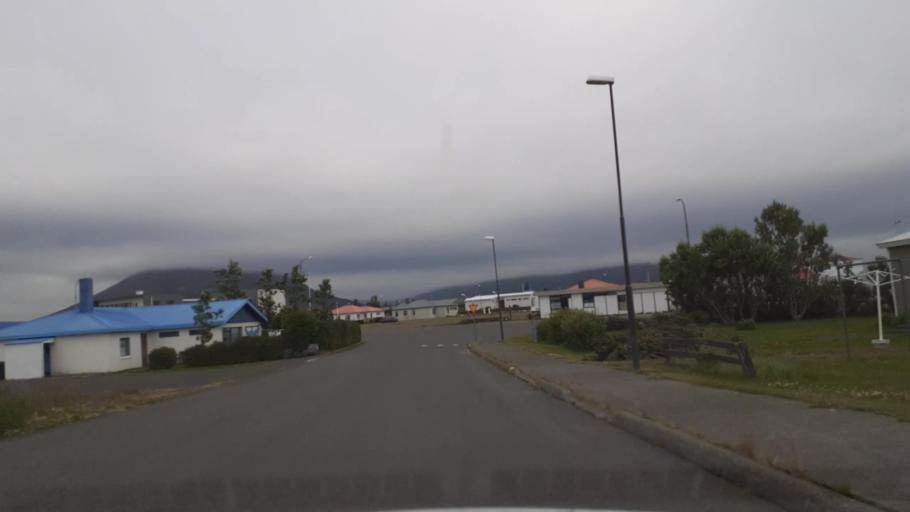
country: IS
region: Northwest
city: Saudarkrokur
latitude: 65.8981
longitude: -19.4131
